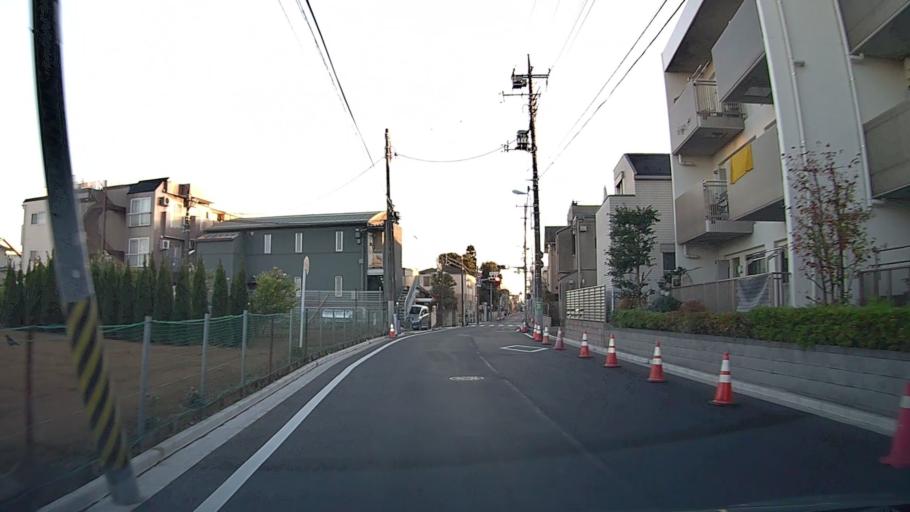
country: JP
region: Tokyo
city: Musashino
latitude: 35.7241
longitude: 139.6102
